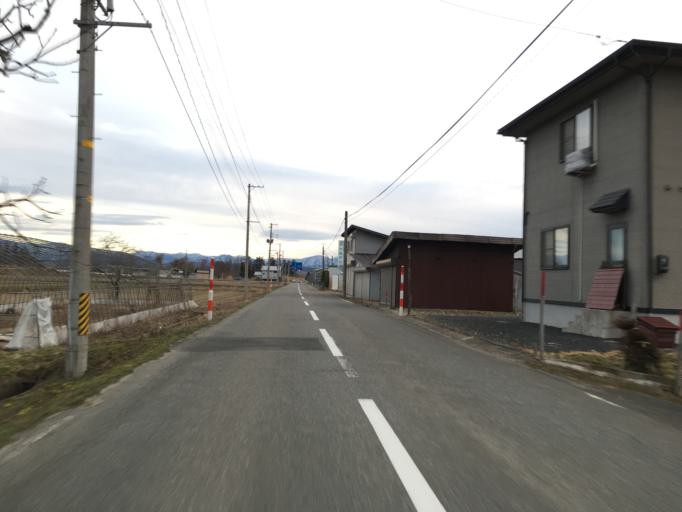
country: JP
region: Yamagata
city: Nagai
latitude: 38.0123
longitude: 140.0787
